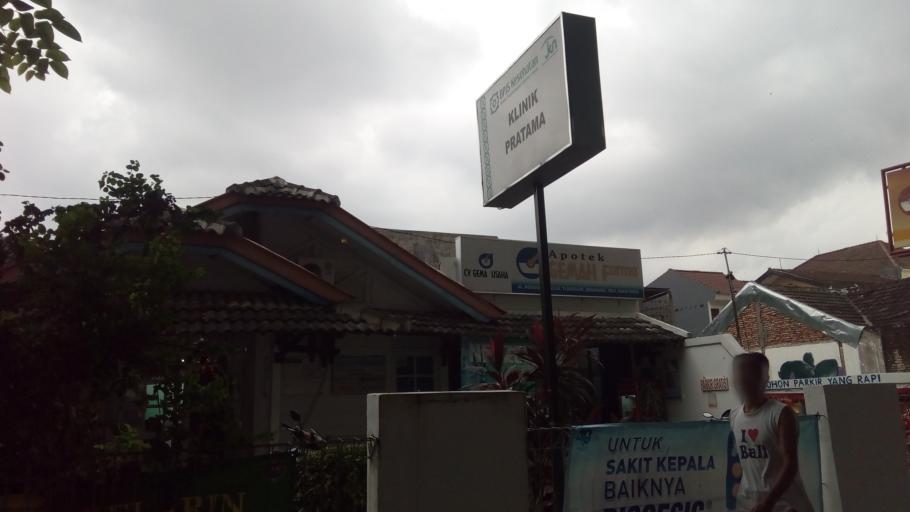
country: ID
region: Central Java
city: Semarang
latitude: -6.9800
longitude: 110.4625
